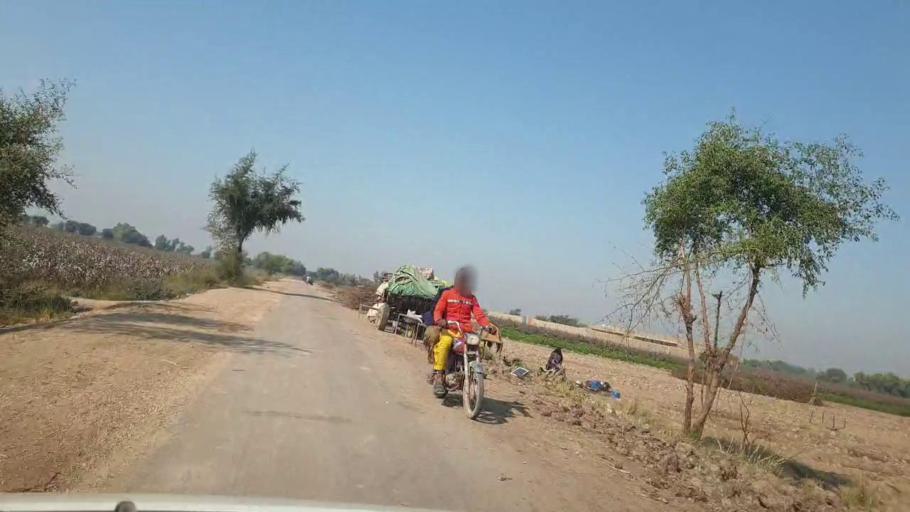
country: PK
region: Sindh
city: Bhan
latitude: 26.6034
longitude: 67.7410
